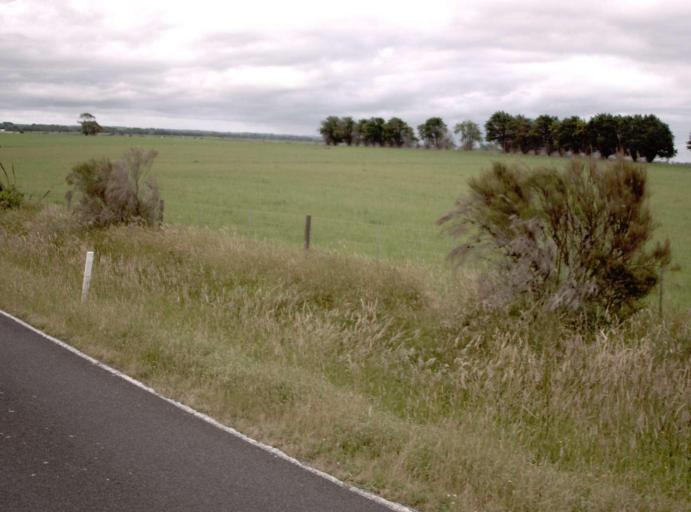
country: AU
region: Victoria
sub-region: Bass Coast
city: North Wonthaggi
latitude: -38.5440
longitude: 145.6973
